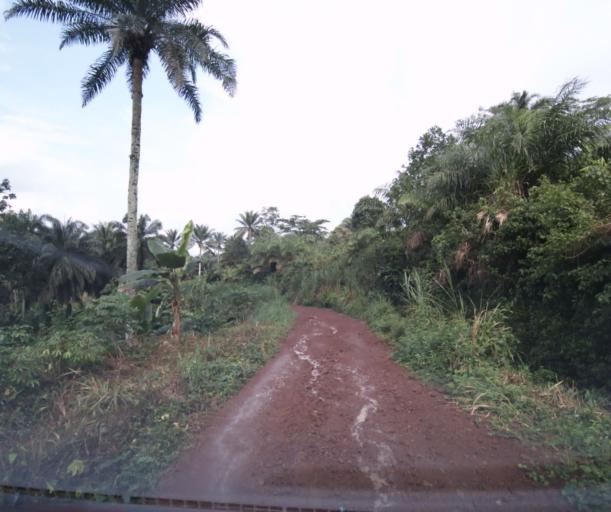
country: CM
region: Littoral
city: Melong
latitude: 5.0595
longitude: 9.9710
